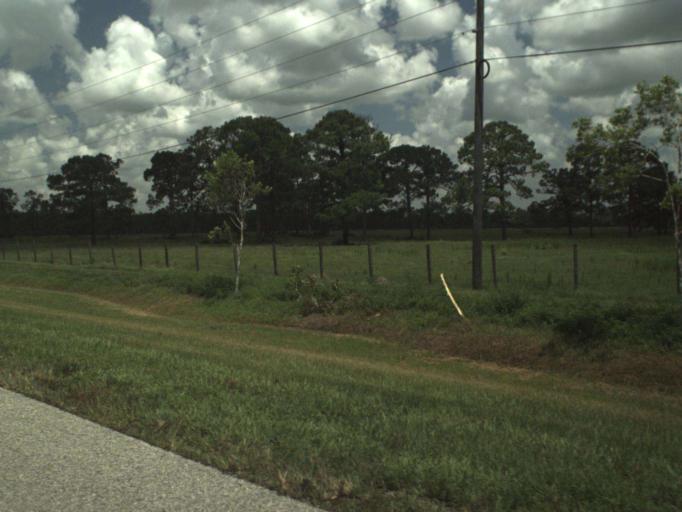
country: US
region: Florida
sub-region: Indian River County
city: Fellsmere
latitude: 27.6816
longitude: -80.8422
